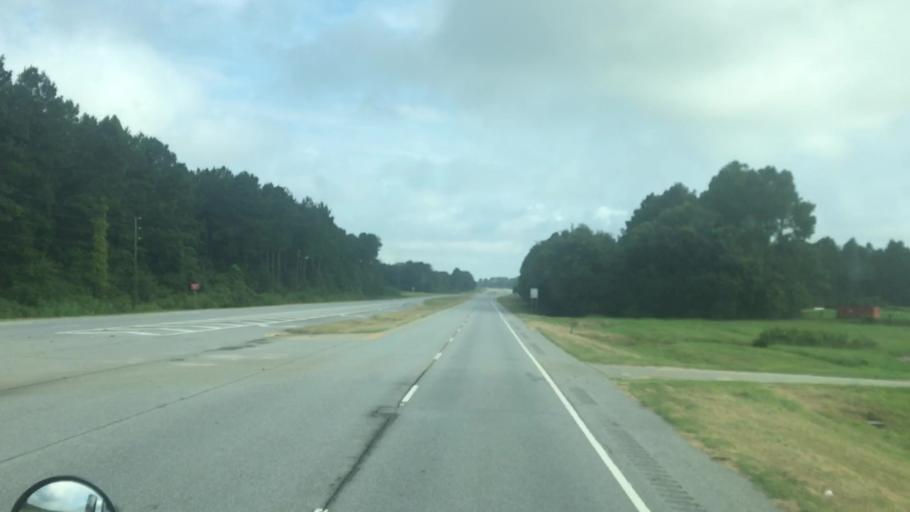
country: US
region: Georgia
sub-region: Miller County
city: Colquitt
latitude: 31.1964
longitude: -84.7676
